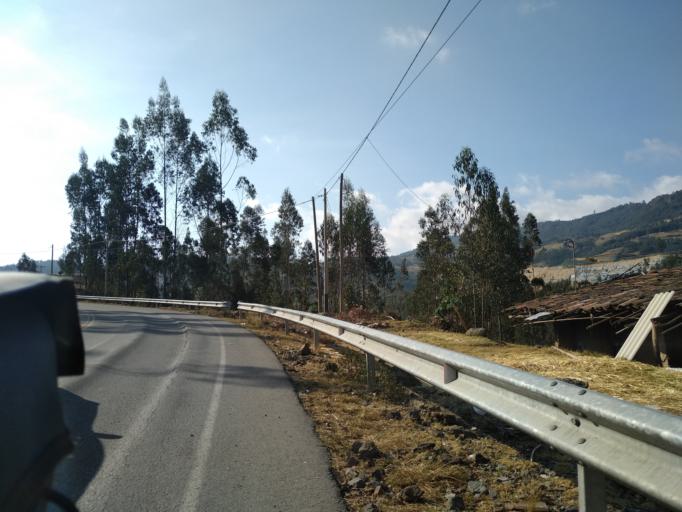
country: PE
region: La Libertad
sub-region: Provincia de Otuzco
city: Agallpampa
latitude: -7.9960
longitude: -78.5088
